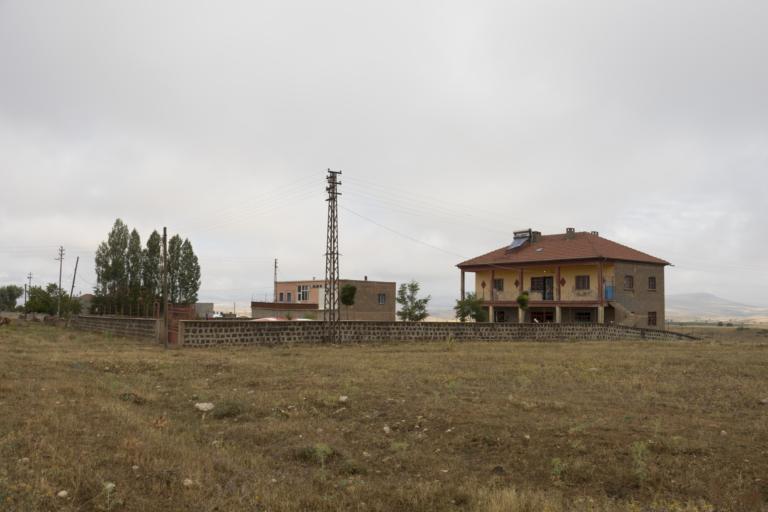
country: TR
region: Kayseri
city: Toklar
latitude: 38.4082
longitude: 36.0852
